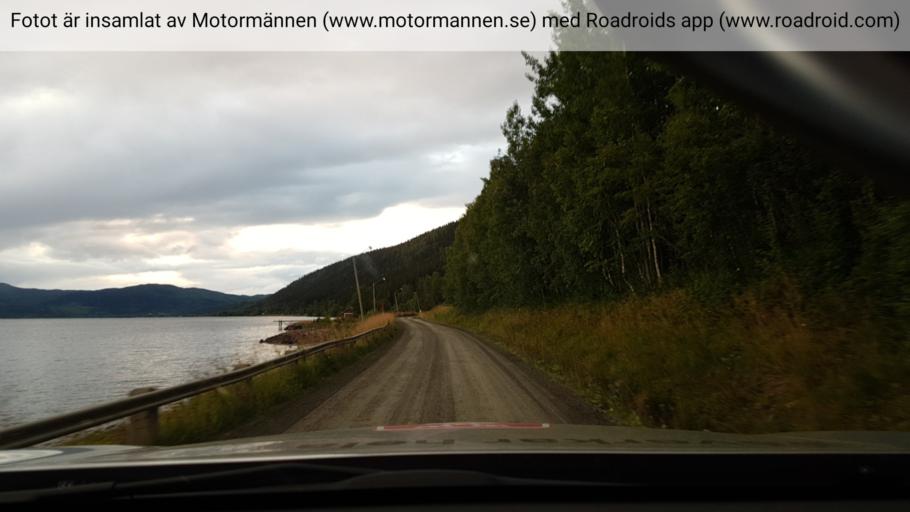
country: NO
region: Nordland
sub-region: Hattfjelldal
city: Hattfjelldal
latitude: 65.6292
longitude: 15.2282
